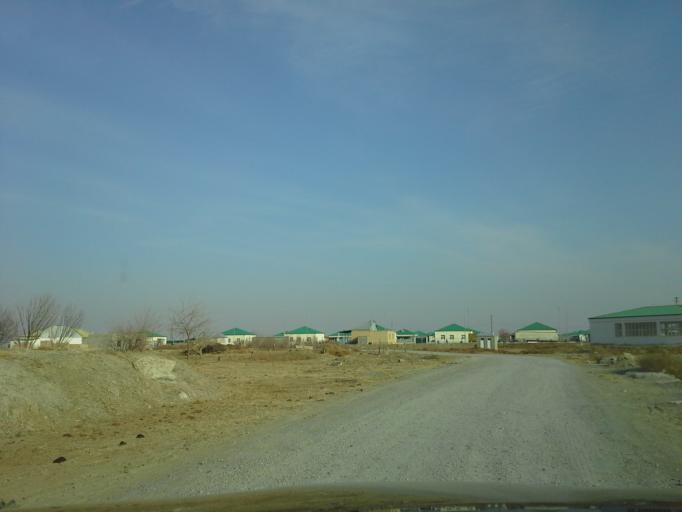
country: TM
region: Ahal
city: Abadan
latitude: 38.1740
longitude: 58.0449
